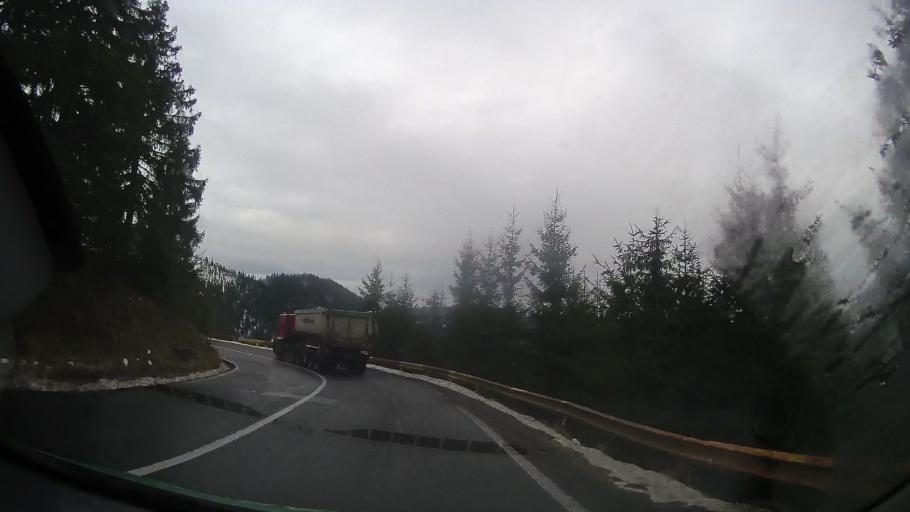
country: RO
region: Harghita
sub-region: Municipiul Gheorgheni
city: Gheorgheni
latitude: 46.7717
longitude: 25.7008
